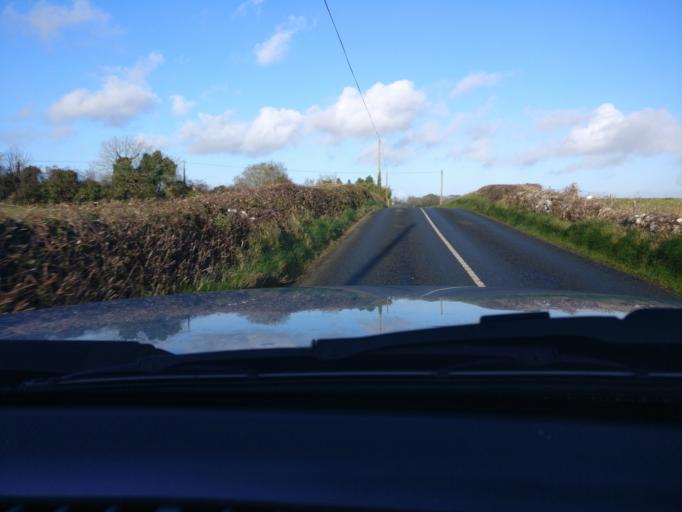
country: IE
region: Leinster
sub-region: An Iarmhi
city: Kilbeggan
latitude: 53.4247
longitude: -7.5614
